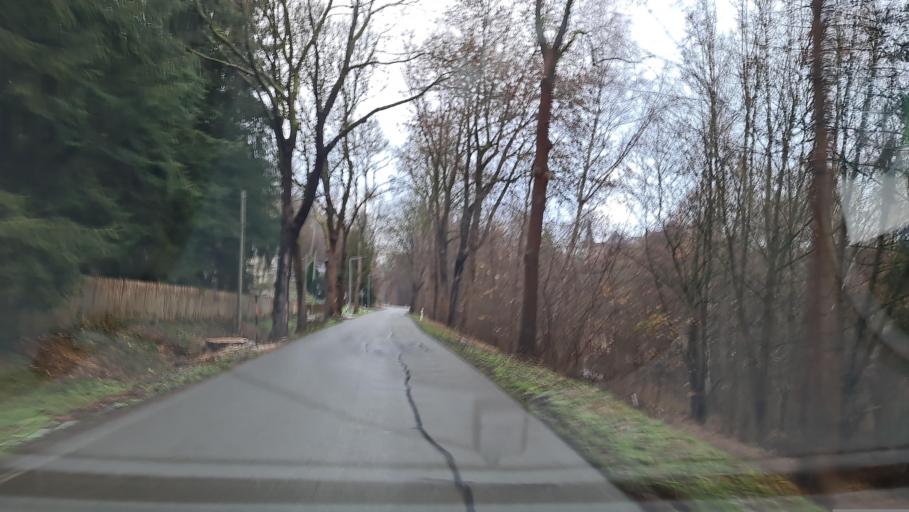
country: DE
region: Saxony
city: Mylau
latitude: 50.6143
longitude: 12.2664
